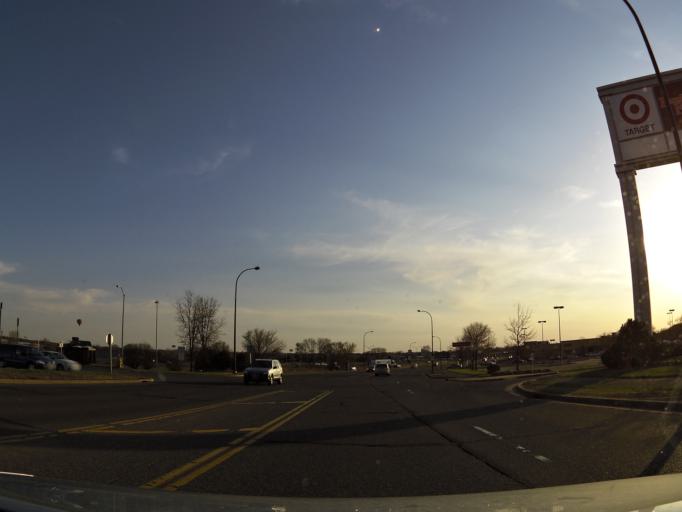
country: US
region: Wisconsin
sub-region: Saint Croix County
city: Hudson
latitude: 44.9649
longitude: -92.7230
